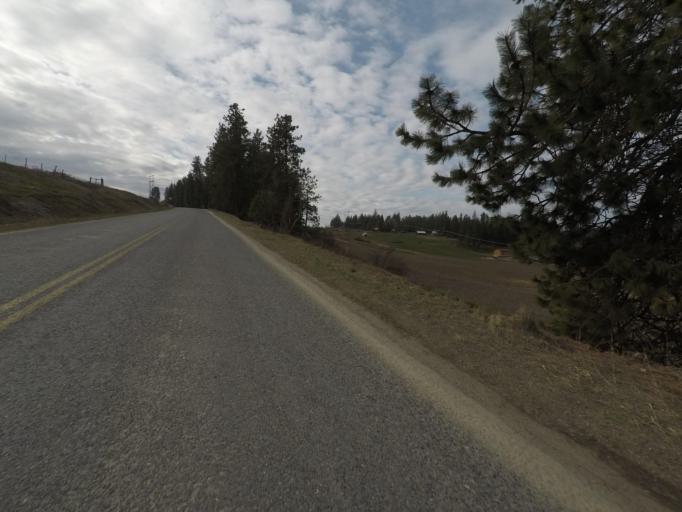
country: US
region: Washington
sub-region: Stevens County
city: Colville
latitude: 48.5301
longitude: -117.8796
